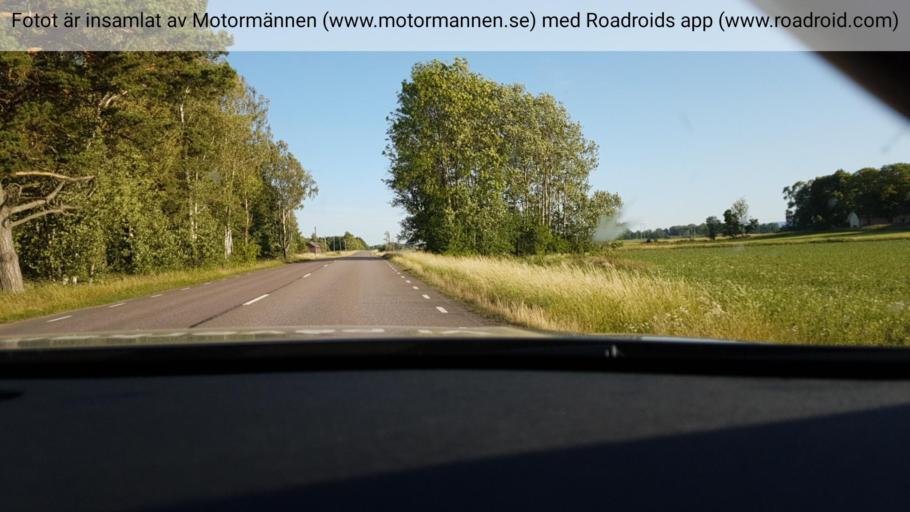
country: SE
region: Vaestra Goetaland
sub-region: Toreboda Kommun
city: Toereboda
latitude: 58.6012
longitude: 14.0095
